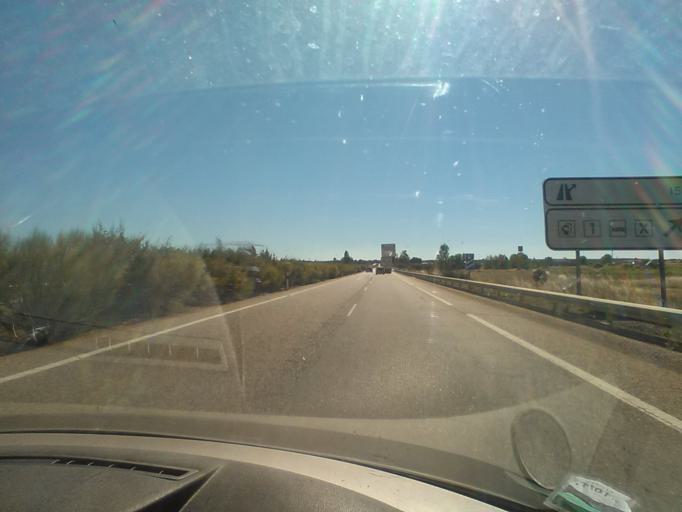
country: ES
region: Castille and Leon
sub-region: Provincia de Zamora
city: Quintanilla de Urz
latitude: 42.0235
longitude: -5.8442
